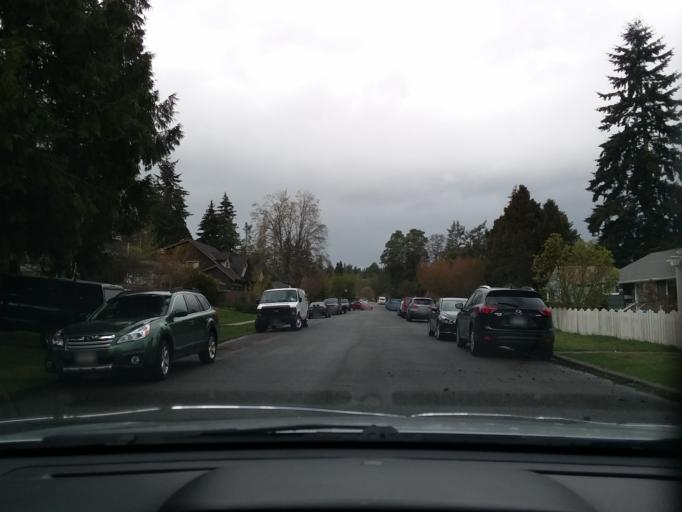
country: US
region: Washington
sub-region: King County
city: Shoreline
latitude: 47.7453
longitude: -122.3197
